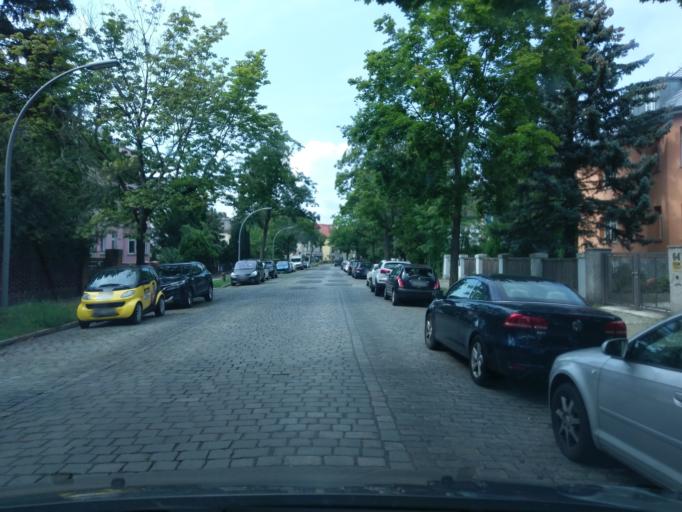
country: DE
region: Berlin
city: Lichterfelde
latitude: 52.4314
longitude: 13.2879
